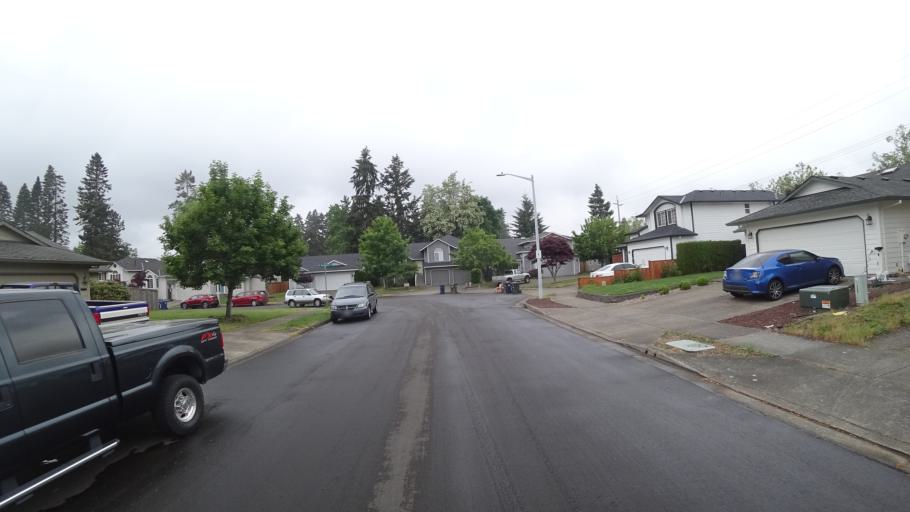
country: US
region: Oregon
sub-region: Washington County
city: Rockcreek
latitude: 45.5317
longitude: -122.8896
